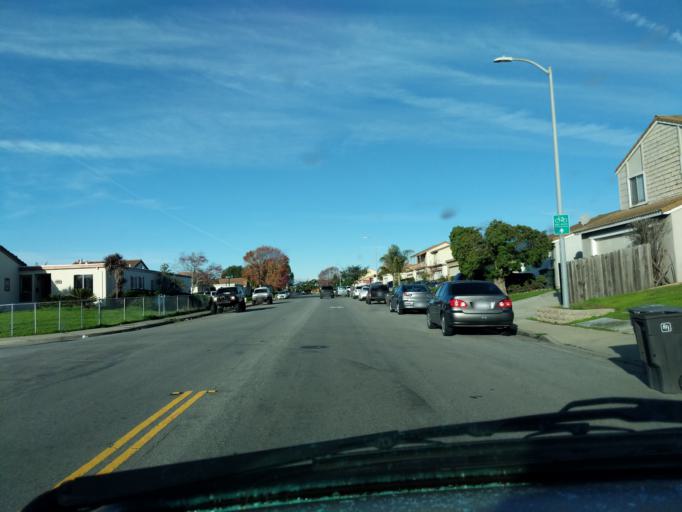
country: US
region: California
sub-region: Monterey County
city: Boronda
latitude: 36.7092
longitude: -121.6601
